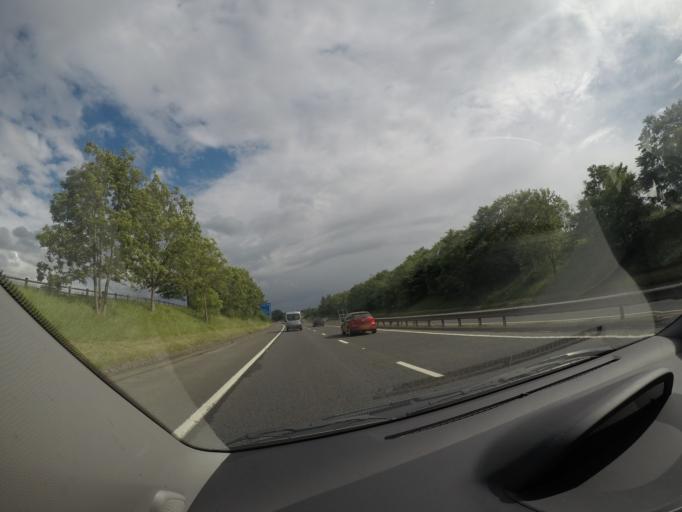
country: GB
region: Scotland
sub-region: Stirling
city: Stirling
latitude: 56.0872
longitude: -3.9440
